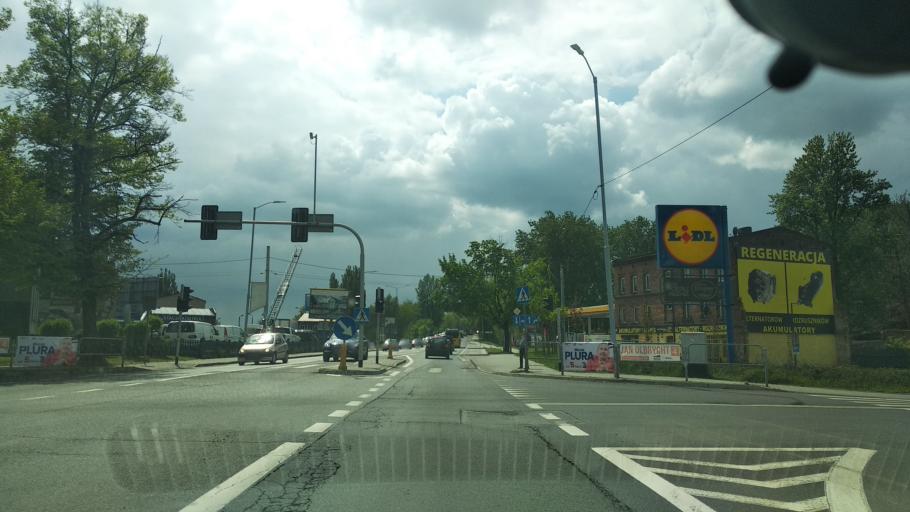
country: PL
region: Silesian Voivodeship
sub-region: Katowice
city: Katowice
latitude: 50.2340
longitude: 18.9767
